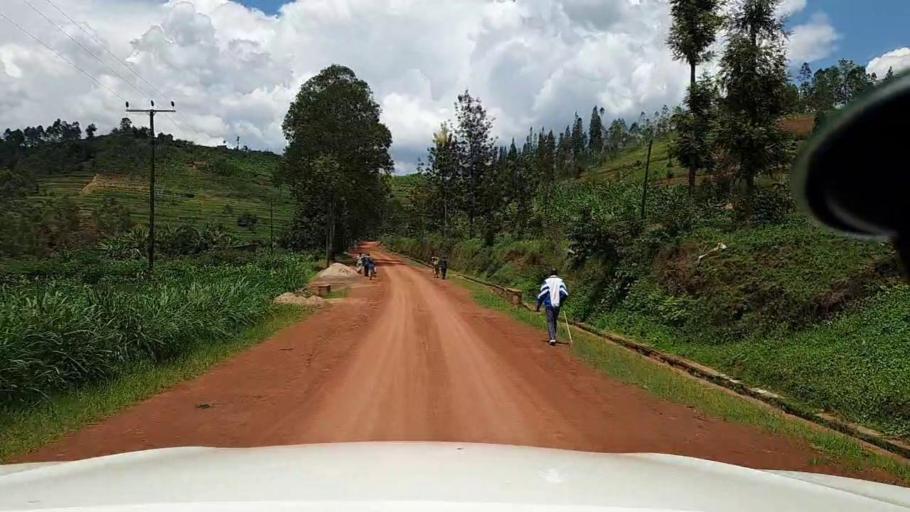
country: RW
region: Northern Province
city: Byumba
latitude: -1.6954
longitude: 29.8282
